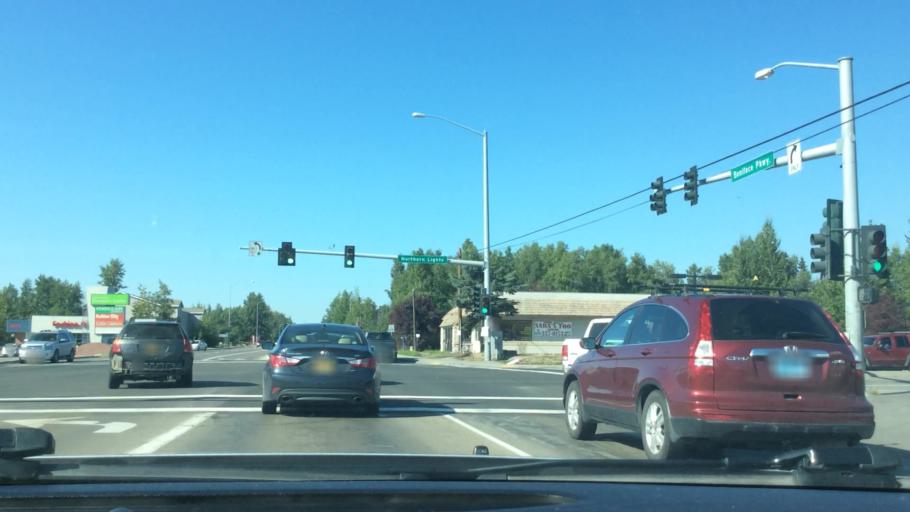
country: US
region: Alaska
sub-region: Anchorage Municipality
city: Anchorage
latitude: 61.1949
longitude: -149.7783
